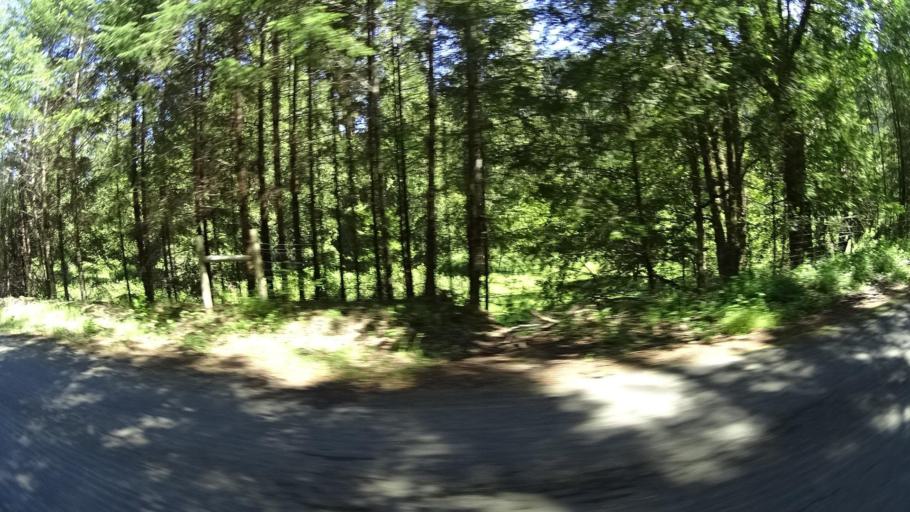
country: US
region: California
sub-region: Humboldt County
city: Rio Dell
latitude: 40.2670
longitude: -124.1996
